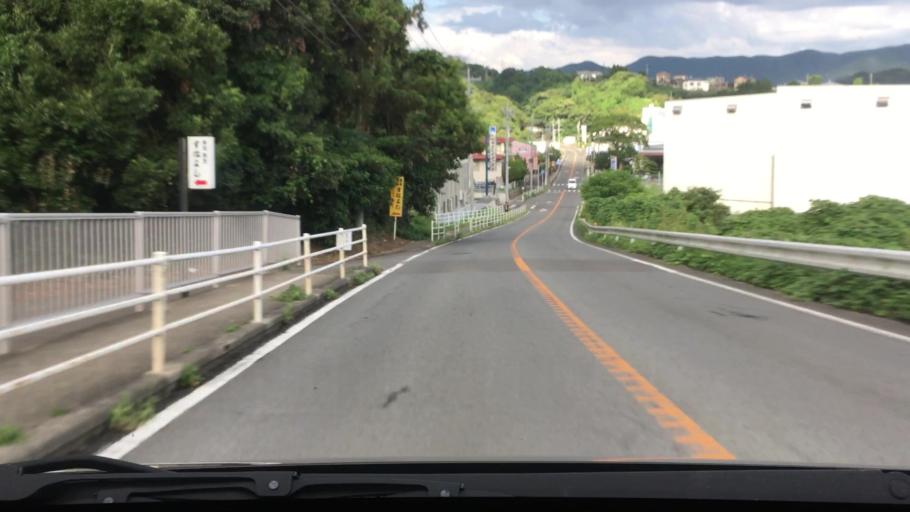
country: JP
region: Nagasaki
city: Togitsu
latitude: 32.8257
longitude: 129.7637
